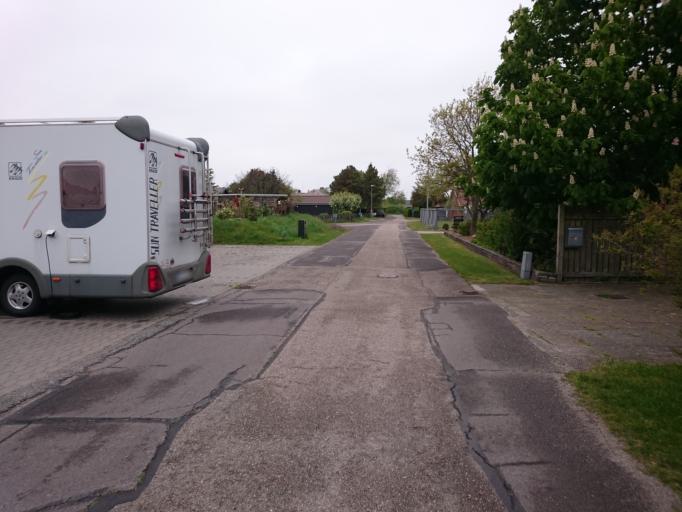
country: DK
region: South Denmark
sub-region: Fano Kommune
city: Nordby
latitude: 55.4481
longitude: 8.3976
